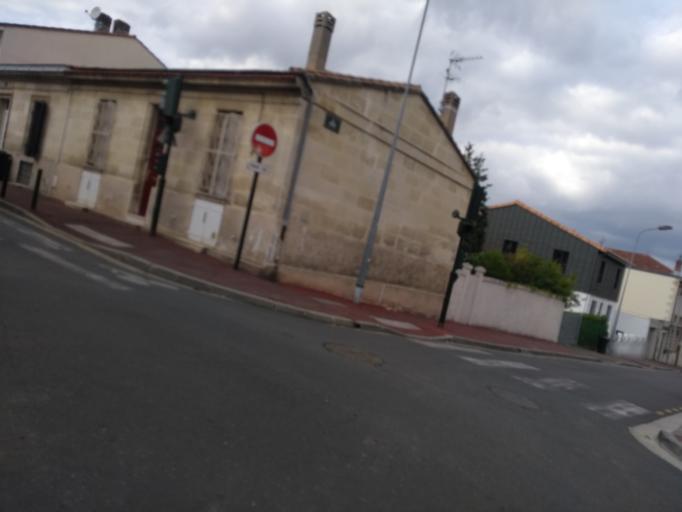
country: FR
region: Aquitaine
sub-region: Departement de la Gironde
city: Begles
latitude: 44.8101
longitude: -0.5694
